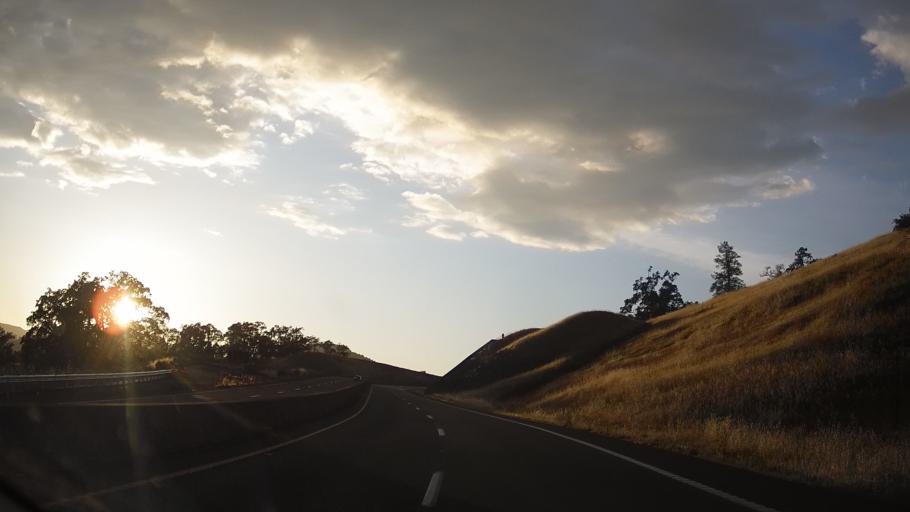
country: US
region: California
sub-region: Mendocino County
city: Redwood Valley
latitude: 39.3145
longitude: -123.2990
